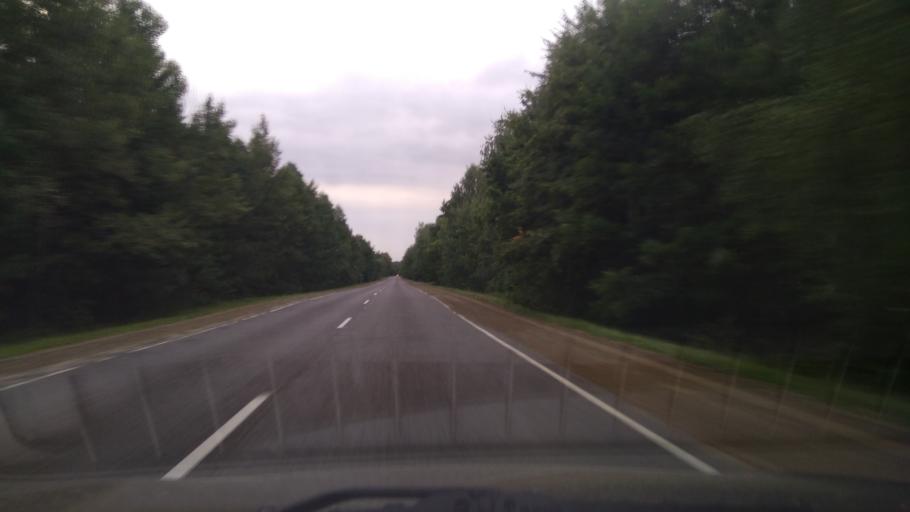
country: BY
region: Brest
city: Byaroza
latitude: 52.4076
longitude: 24.9971
